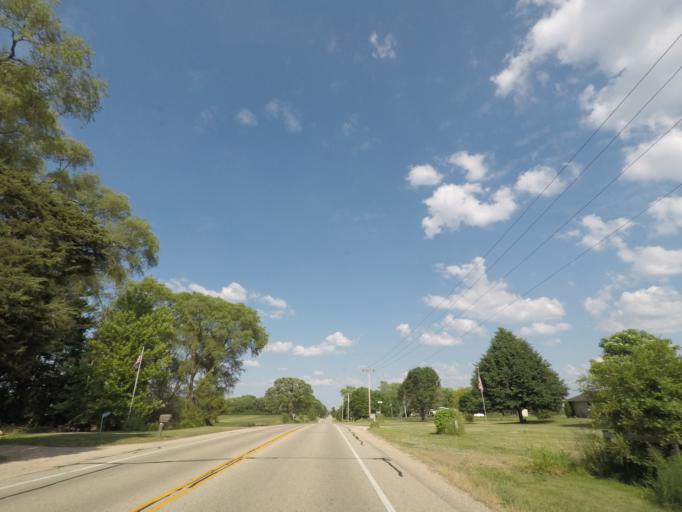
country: US
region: Wisconsin
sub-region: Waukesha County
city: Eagle
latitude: 42.7932
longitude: -88.4938
